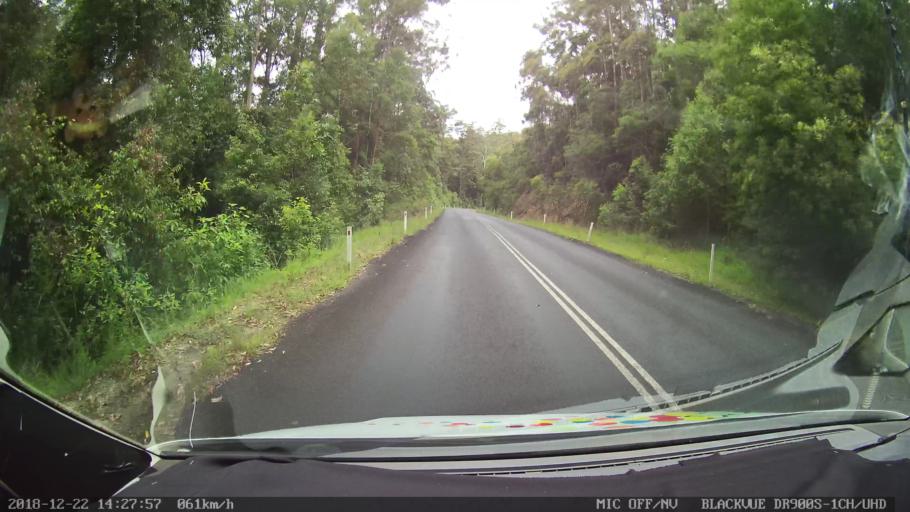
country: AU
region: New South Wales
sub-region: Bellingen
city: Dorrigo
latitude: -30.0694
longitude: 152.6355
